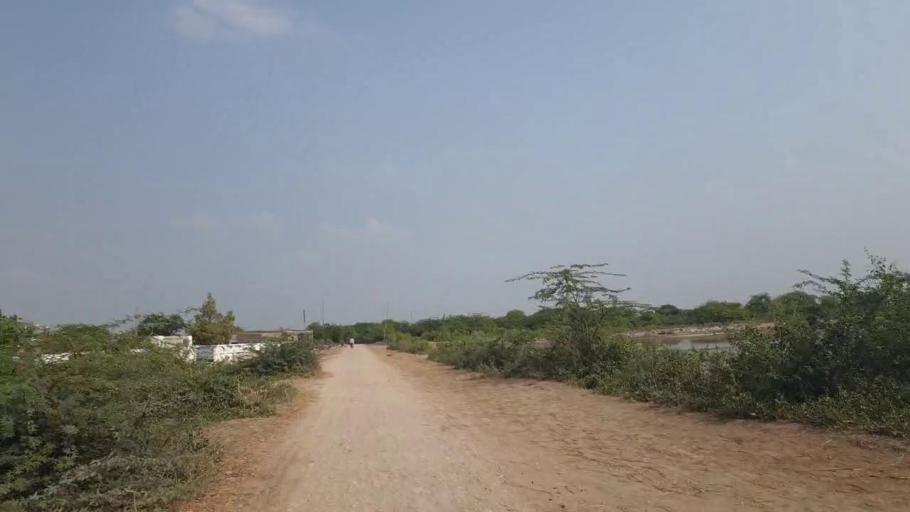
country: PK
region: Sindh
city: Badin
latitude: 24.5496
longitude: 68.7276
